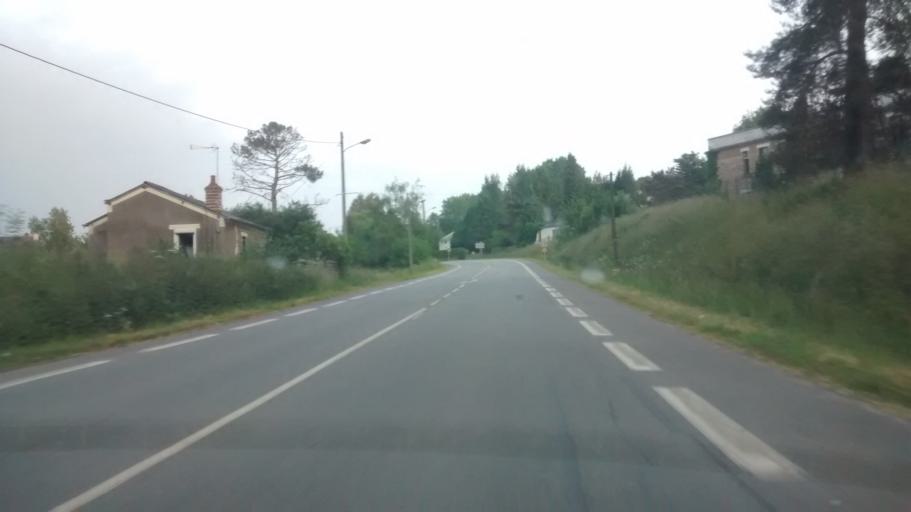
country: FR
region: Brittany
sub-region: Departement du Morbihan
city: Beignon
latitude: 47.9499
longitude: -2.1352
